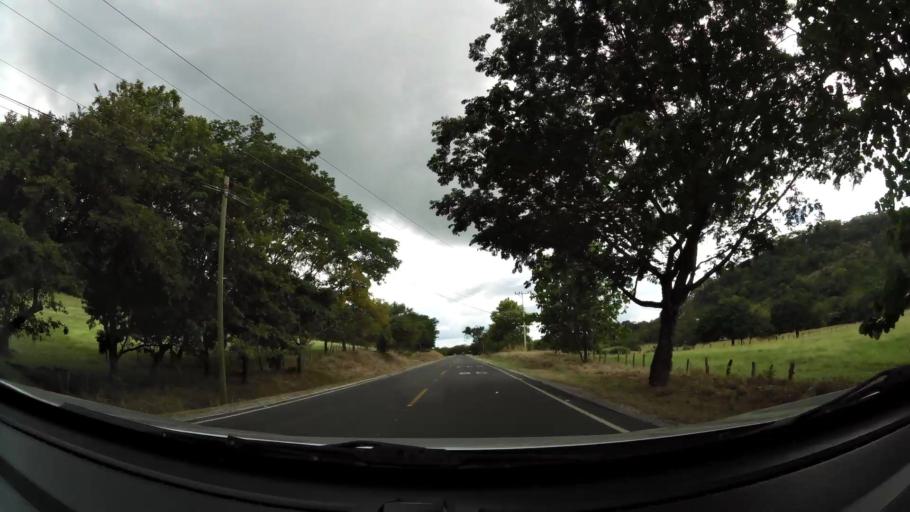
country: CR
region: Guanacaste
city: Nandayure
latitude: 10.2270
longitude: -85.2178
